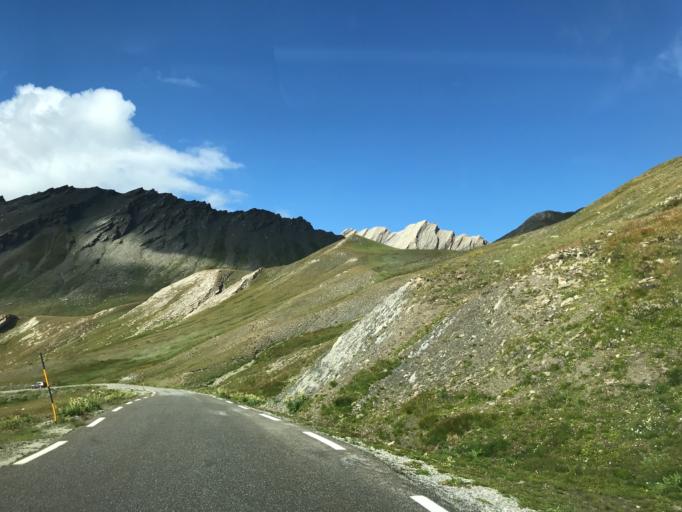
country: IT
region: Piedmont
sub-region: Provincia di Cuneo
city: Pontechianale
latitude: 44.6863
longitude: 6.9787
